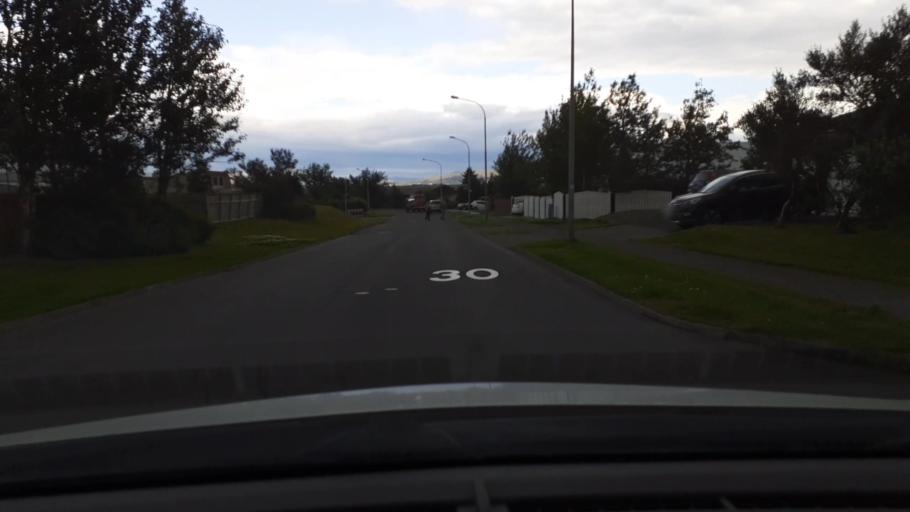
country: IS
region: Capital Region
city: Reykjavik
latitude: 64.2401
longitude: -21.8361
